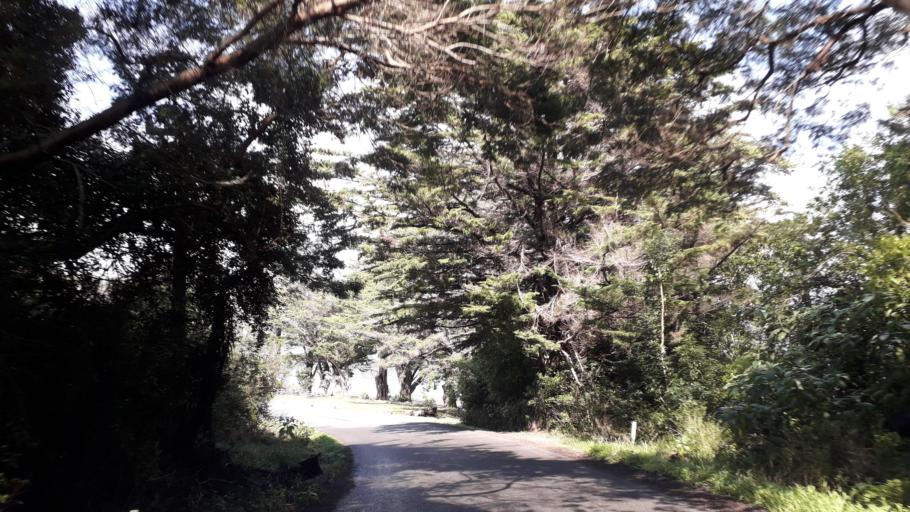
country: NZ
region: Northland
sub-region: Far North District
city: Paihia
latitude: -35.2311
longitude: 174.2610
